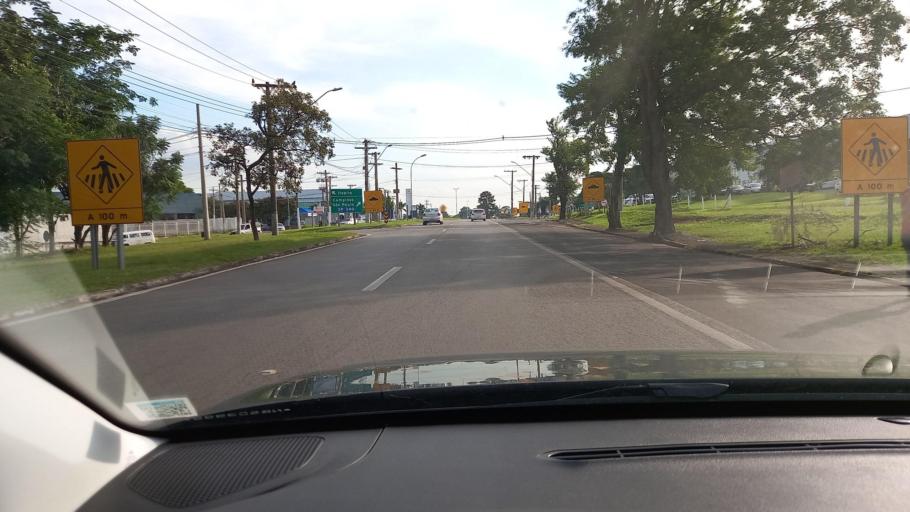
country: BR
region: Sao Paulo
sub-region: Mogi-Mirim
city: Mogi Mirim
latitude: -22.4471
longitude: -46.9783
